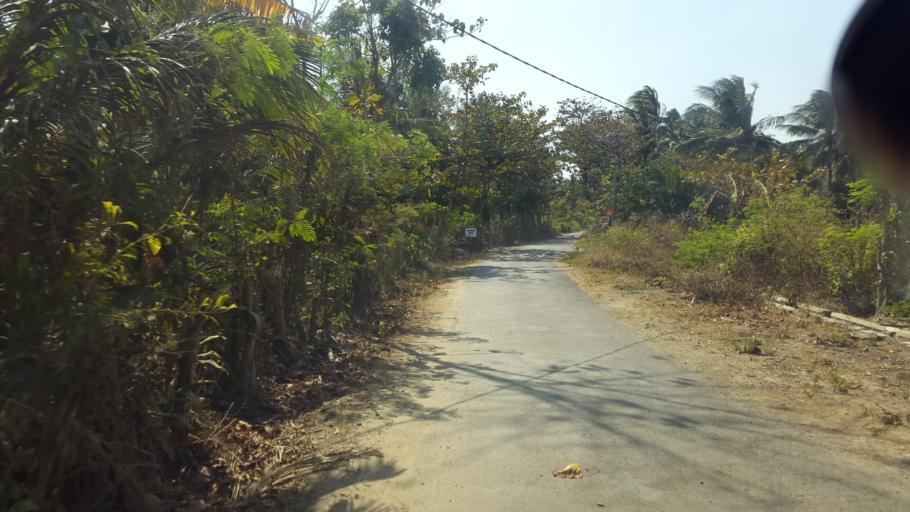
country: ID
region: West Java
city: Gunungbatu
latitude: -7.3405
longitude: 106.4013
